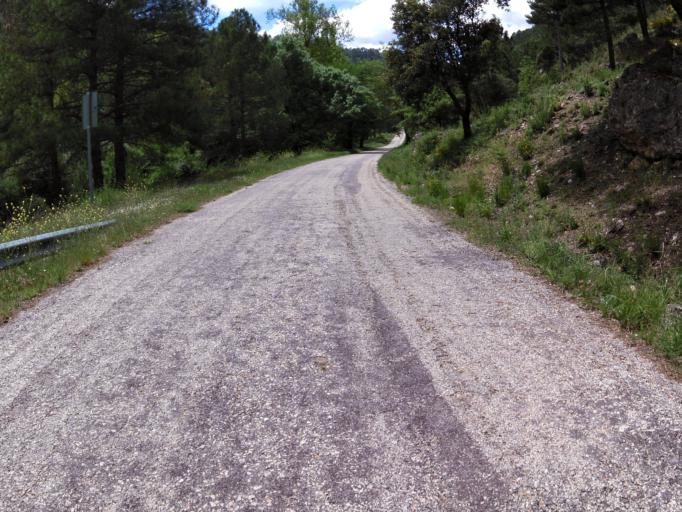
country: ES
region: Castille-La Mancha
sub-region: Provincia de Albacete
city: Paterna del Madera
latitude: 38.5752
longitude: -2.3537
